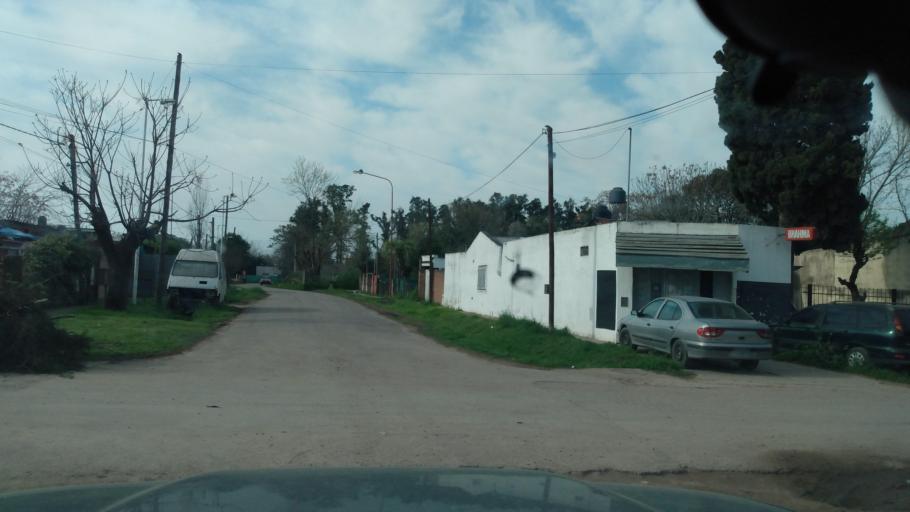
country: AR
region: Buenos Aires
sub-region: Partido de Lujan
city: Lujan
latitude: -34.5500
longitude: -59.1192
